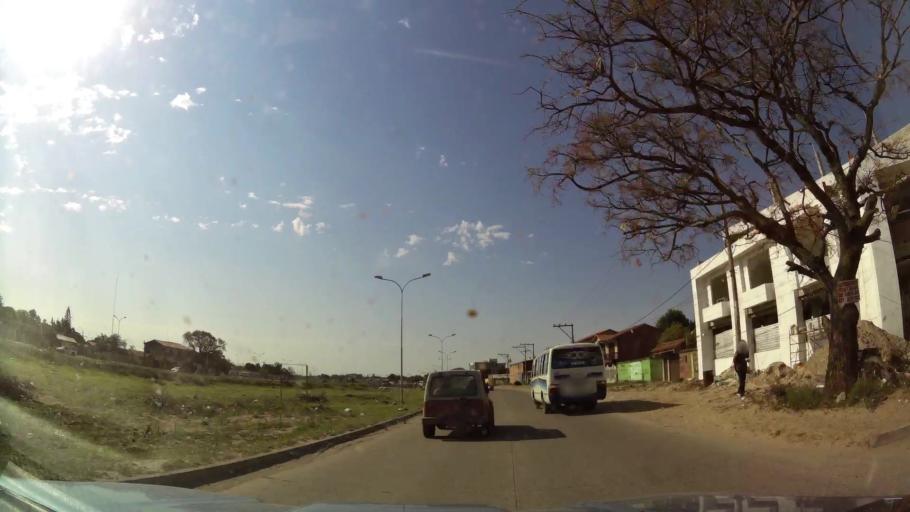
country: BO
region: Santa Cruz
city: Santa Cruz de la Sierra
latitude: -17.8092
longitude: -63.1412
